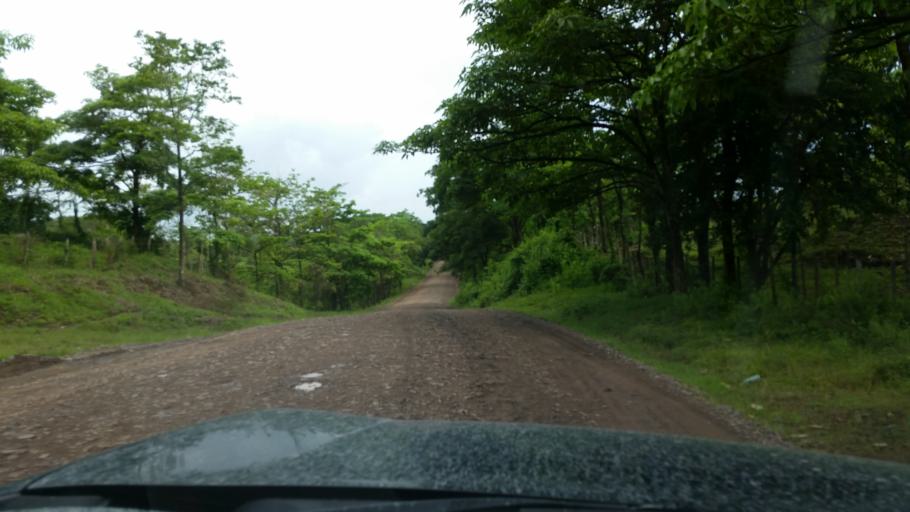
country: NI
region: Atlantico Norte (RAAN)
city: Siuna
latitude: 13.4615
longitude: -84.8494
